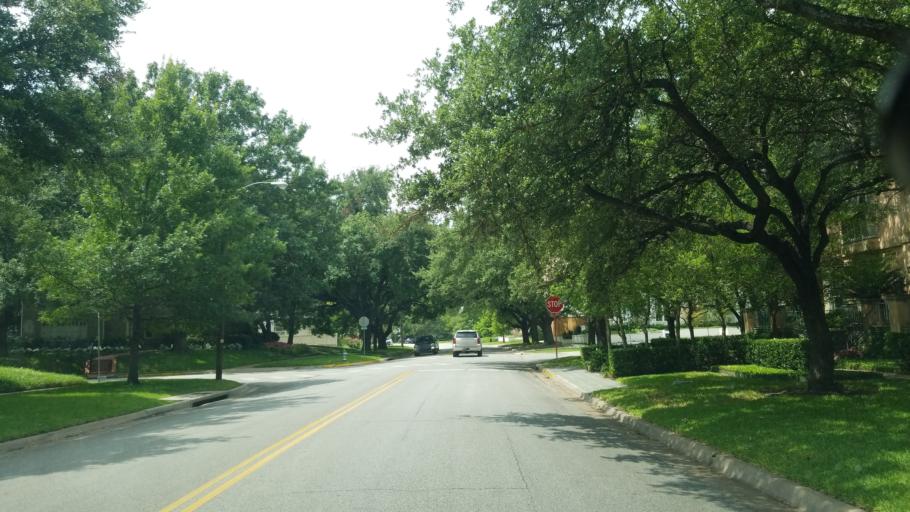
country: US
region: Texas
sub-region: Dallas County
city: University Park
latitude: 32.8419
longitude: -96.8108
